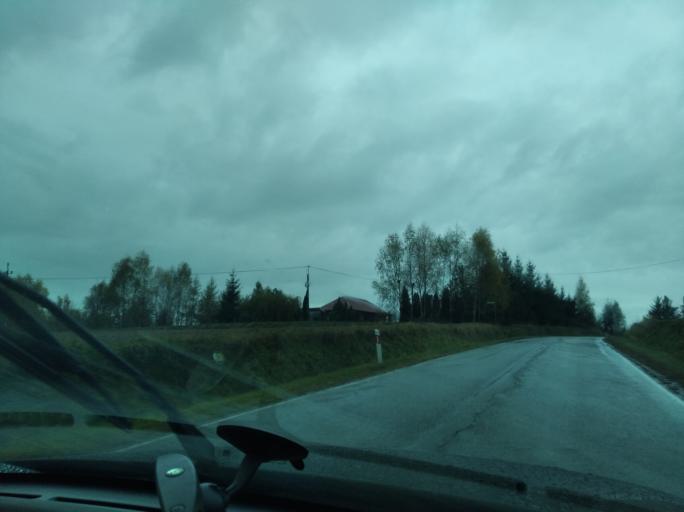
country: PL
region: Subcarpathian Voivodeship
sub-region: Powiat lancucki
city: Handzlowka
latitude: 49.9869
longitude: 22.1900
